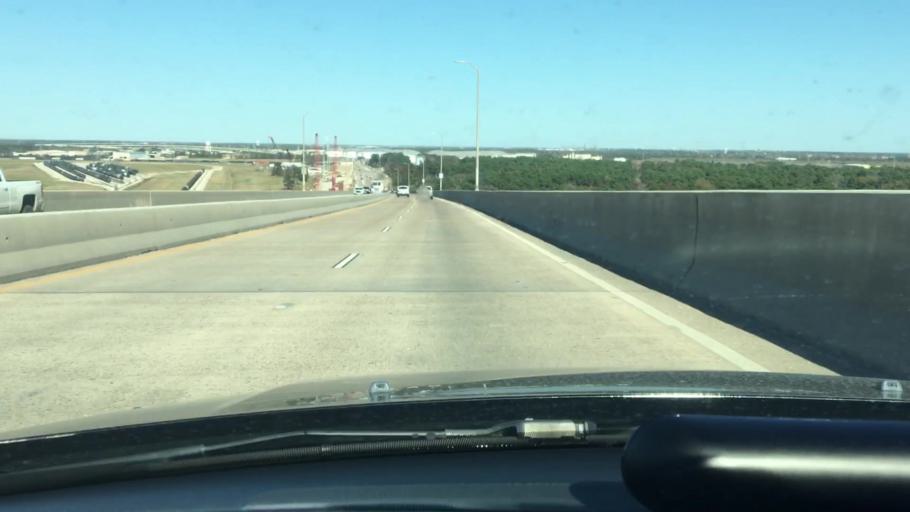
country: US
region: Texas
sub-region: Harris County
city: Deer Park
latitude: 29.7396
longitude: -95.1458
